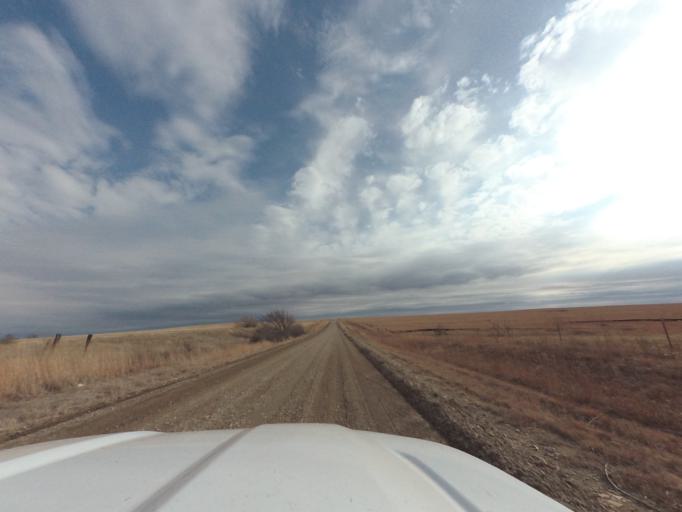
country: US
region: Kansas
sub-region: Chase County
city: Cottonwood Falls
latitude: 38.2171
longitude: -96.7097
